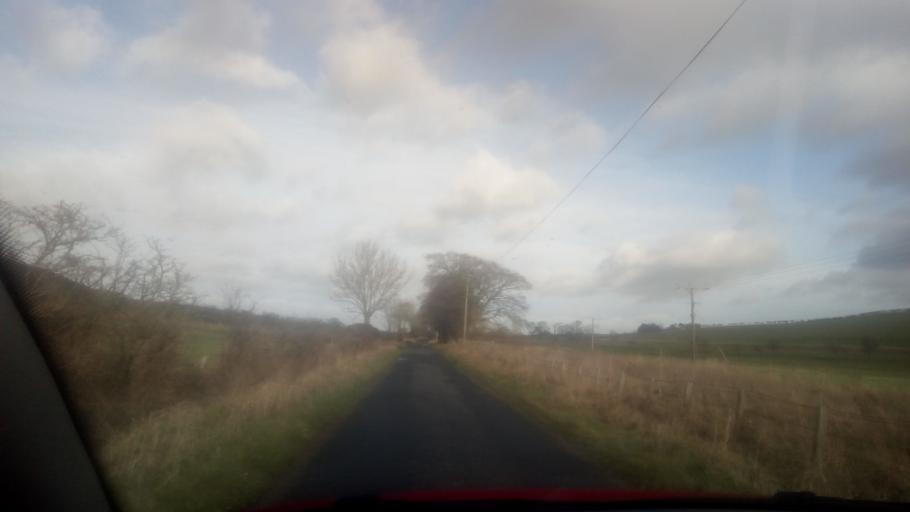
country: GB
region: Scotland
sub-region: The Scottish Borders
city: Kelso
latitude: 55.4971
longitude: -2.4277
